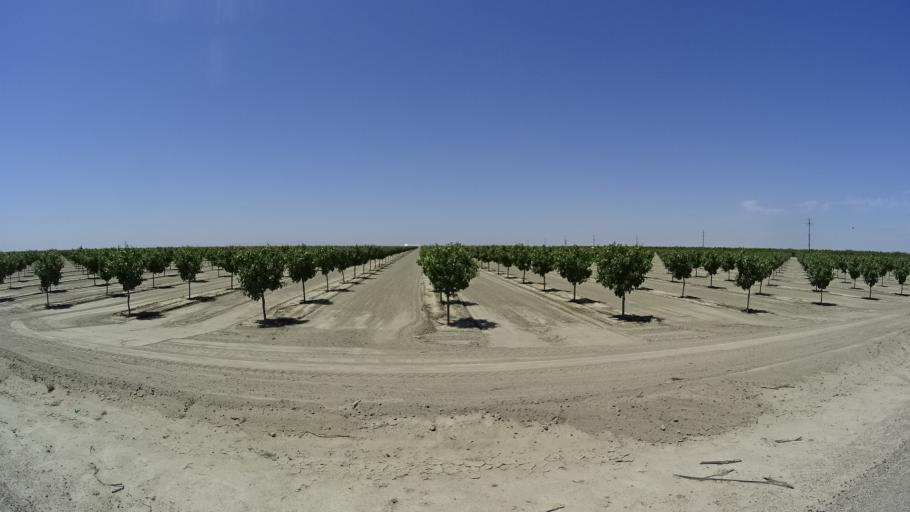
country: US
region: California
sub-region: Kings County
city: Corcoran
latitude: 36.1078
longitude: -119.5990
